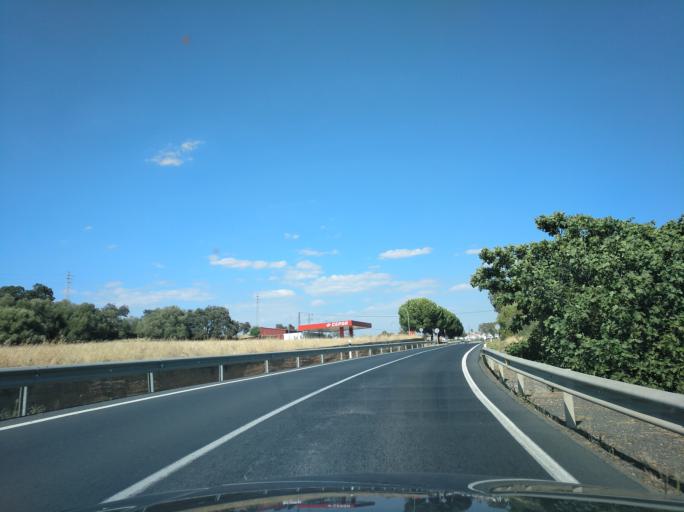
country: ES
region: Andalusia
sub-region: Provincia de Huelva
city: Alosno
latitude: 37.5452
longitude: -7.1250
